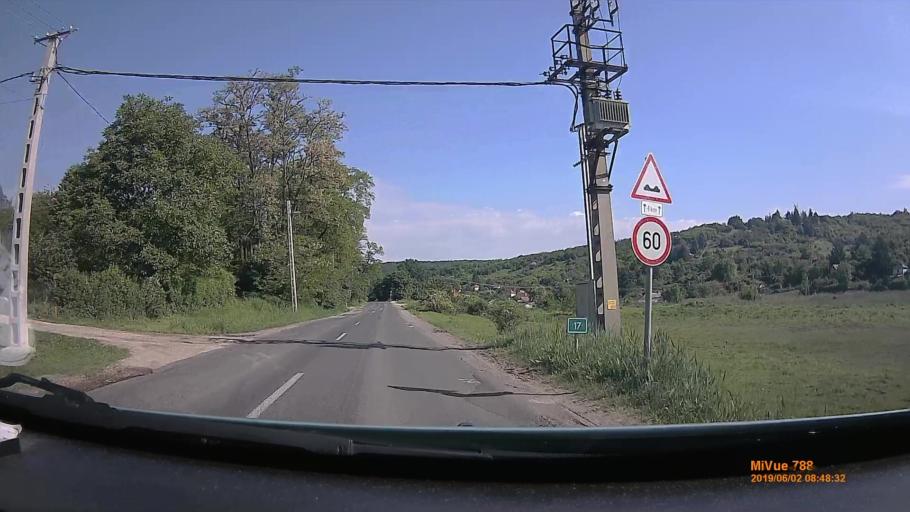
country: HU
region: Borsod-Abauj-Zemplen
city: Sajobabony
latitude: 48.1370
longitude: 20.7042
